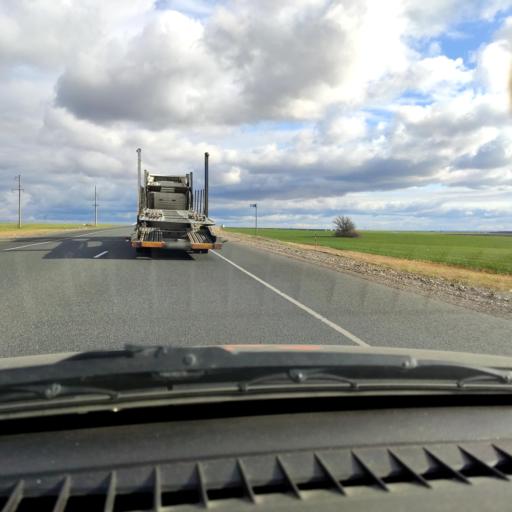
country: RU
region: Samara
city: Varlamovo
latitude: 53.2099
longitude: 48.3940
